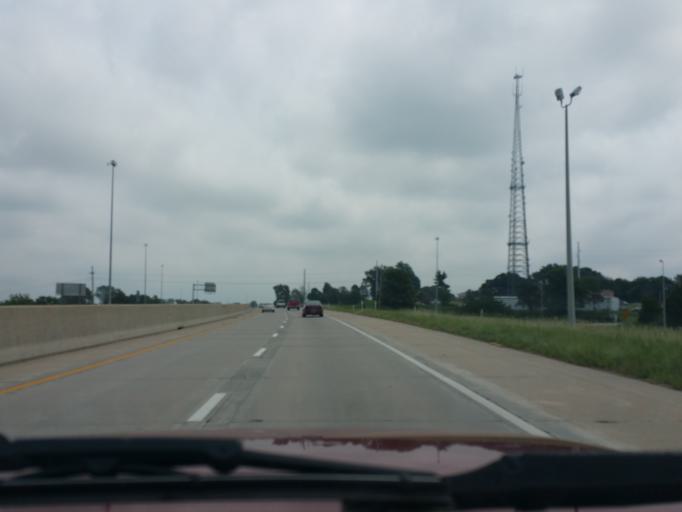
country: US
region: Kansas
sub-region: Shawnee County
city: Topeka
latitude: 39.0674
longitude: -95.7275
